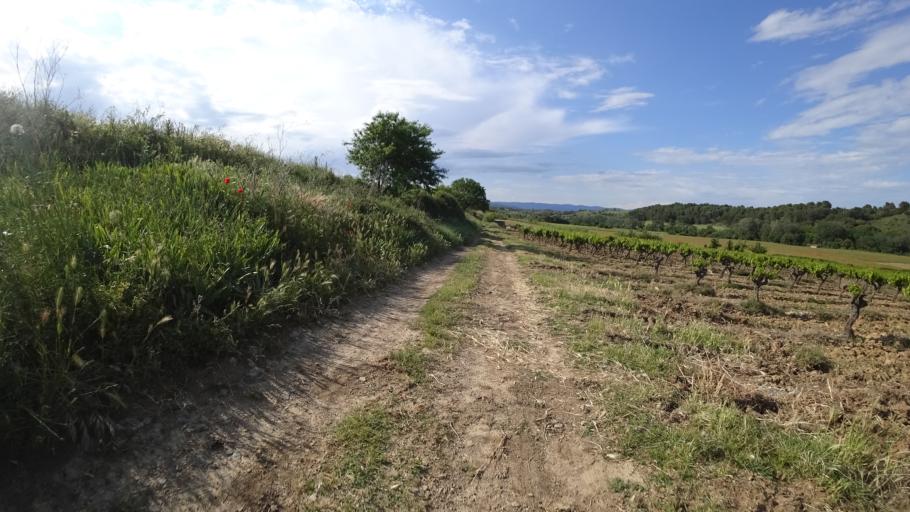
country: FR
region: Languedoc-Roussillon
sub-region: Departement de l'Aude
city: Canet
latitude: 43.2545
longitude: 2.8352
